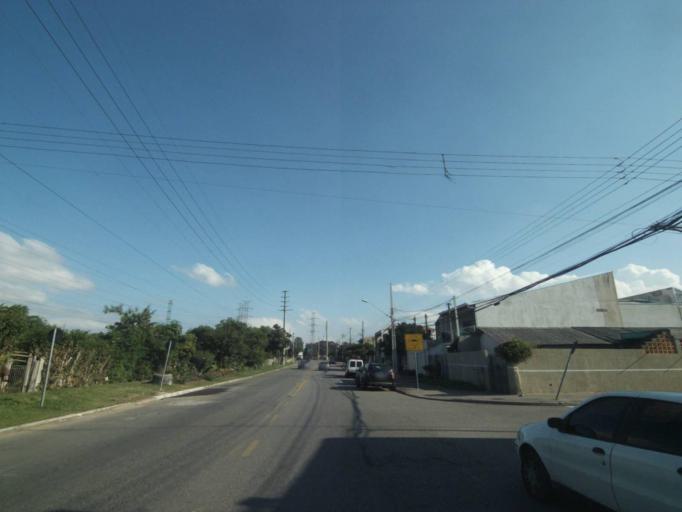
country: BR
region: Parana
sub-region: Araucaria
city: Araucaria
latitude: -25.5311
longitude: -49.3319
